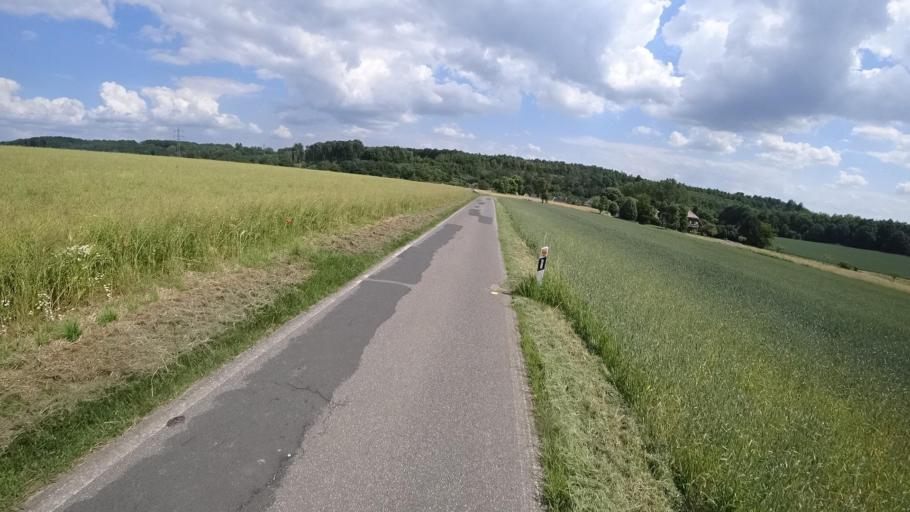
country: DE
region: Rheinland-Pfalz
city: Bachenberg
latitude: 50.7074
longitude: 7.6475
